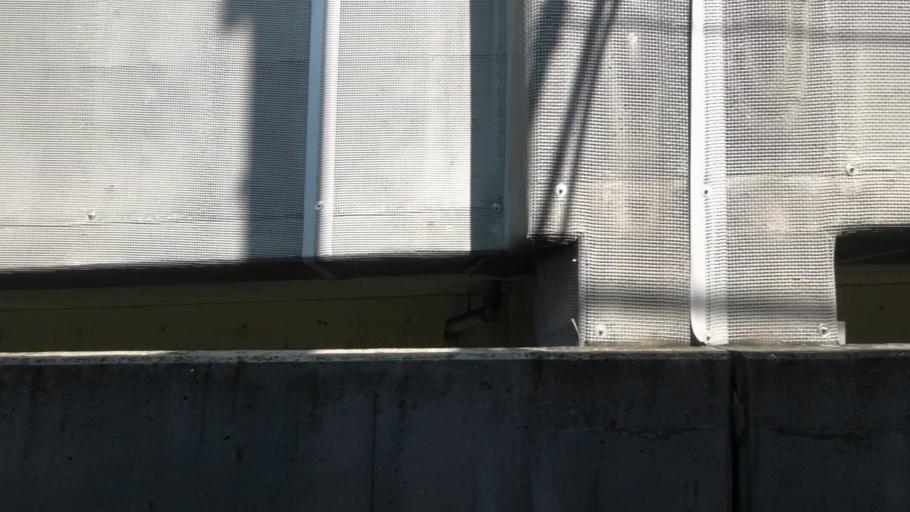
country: JP
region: Kagawa
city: Sakaidecho
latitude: 34.3095
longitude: 133.8159
